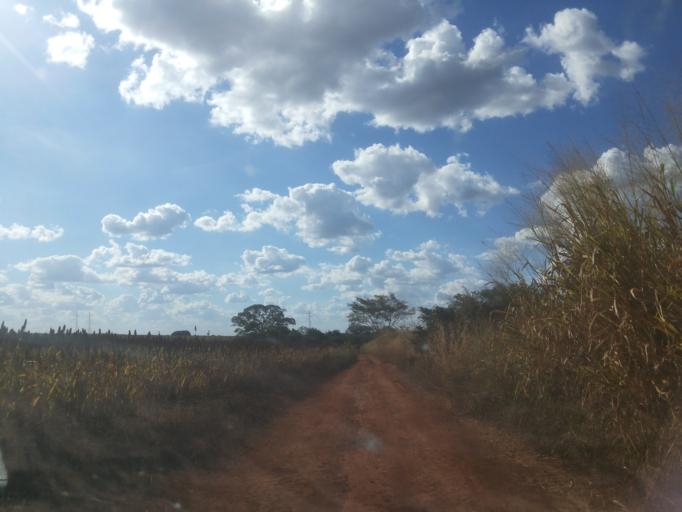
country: BR
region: Minas Gerais
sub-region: Capinopolis
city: Capinopolis
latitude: -18.5978
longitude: -49.4952
